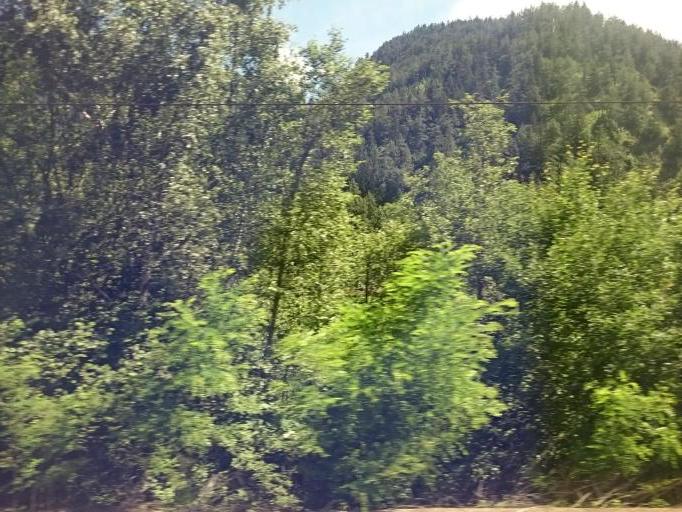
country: IT
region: Trentino-Alto Adige
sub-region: Bolzano
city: Campo di Trens
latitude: 46.8583
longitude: 11.5086
